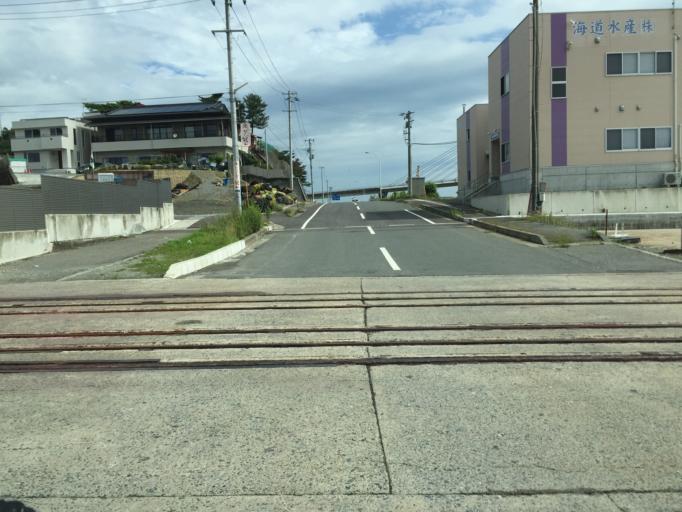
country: JP
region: Miyagi
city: Marumori
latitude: 37.8240
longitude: 140.9729
